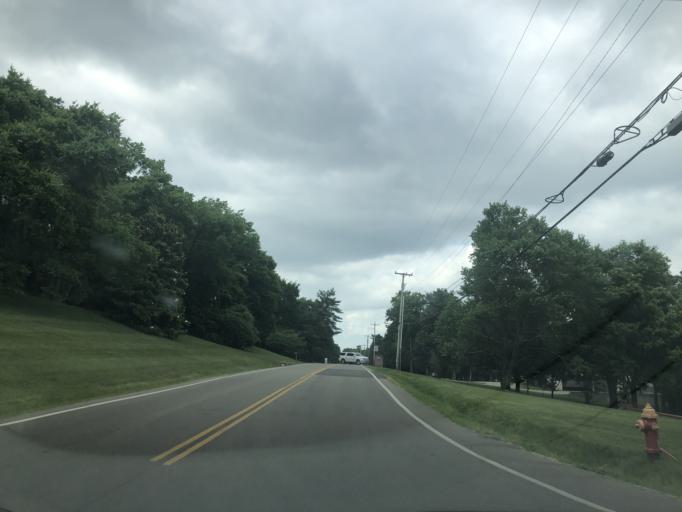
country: US
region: Tennessee
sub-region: Davidson County
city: Forest Hills
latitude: 36.0837
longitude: -86.8206
